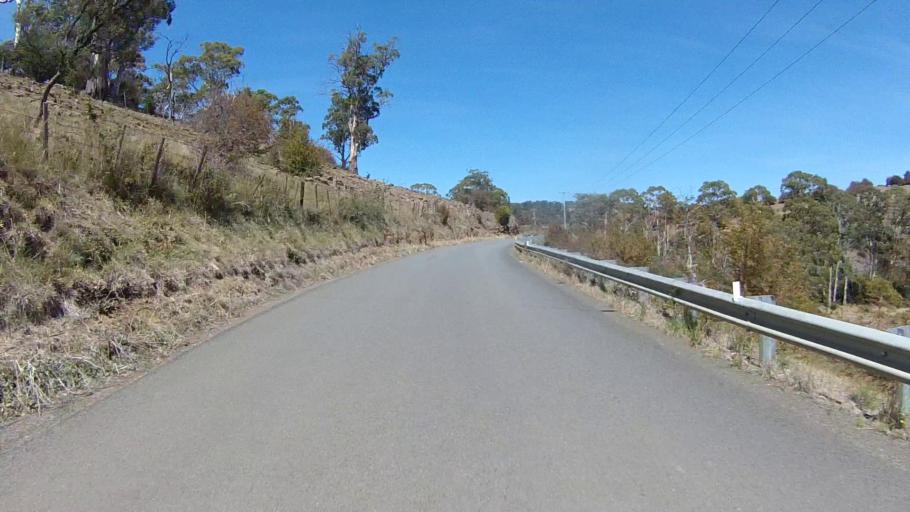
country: AU
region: Tasmania
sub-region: Sorell
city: Sorell
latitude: -42.7599
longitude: 147.6523
